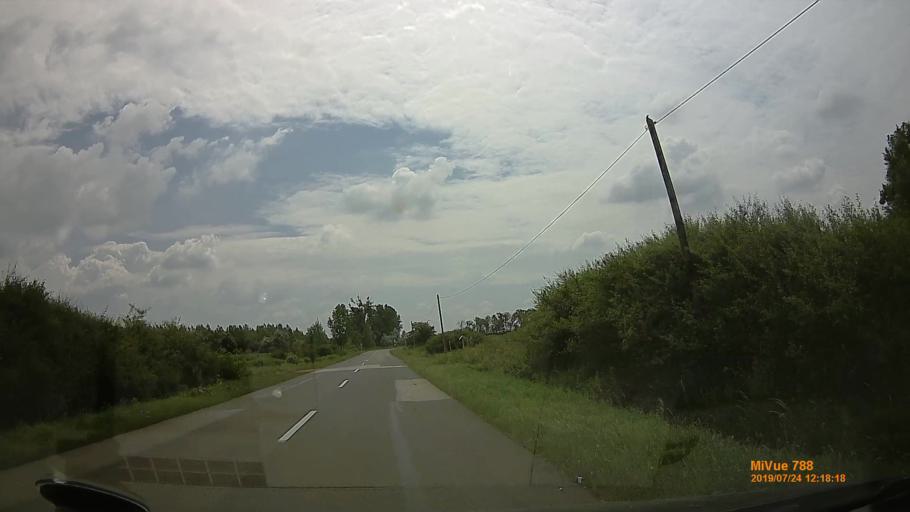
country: HU
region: Szabolcs-Szatmar-Bereg
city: Vasarosnameny
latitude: 48.1524
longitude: 22.3469
